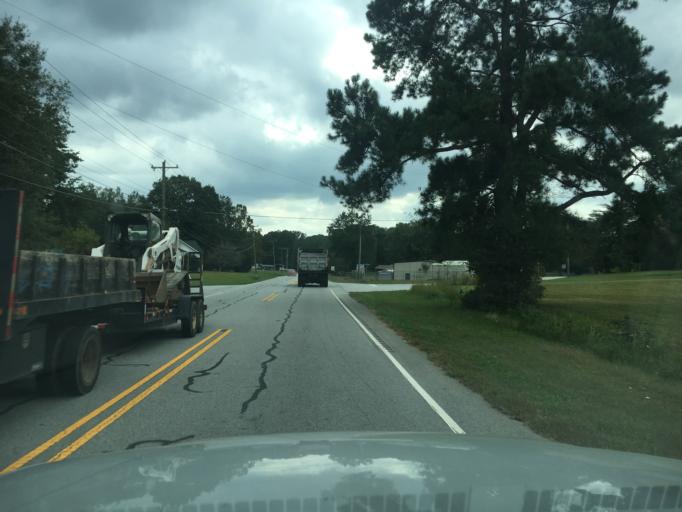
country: US
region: South Carolina
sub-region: Greenville County
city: Greer
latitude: 34.9715
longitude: -82.2385
